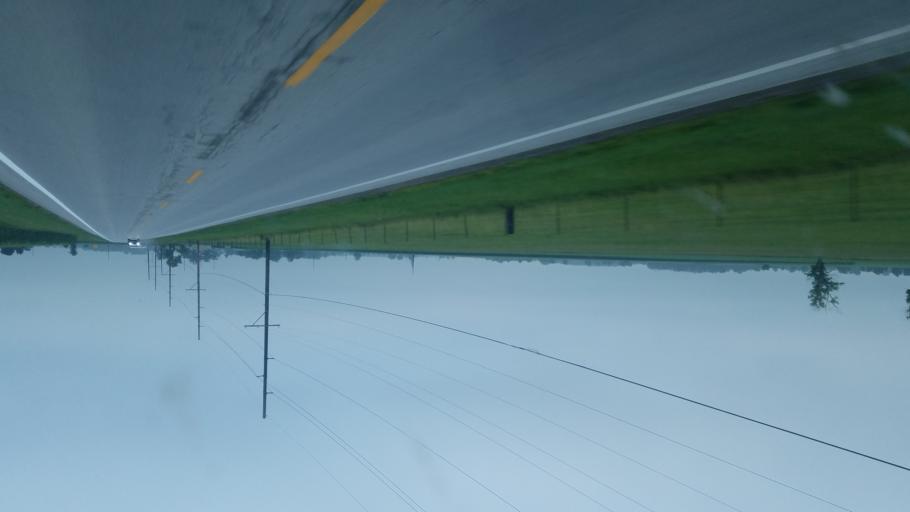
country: US
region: Ohio
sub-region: Fayette County
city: Washington Court House
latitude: 39.5848
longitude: -83.3931
